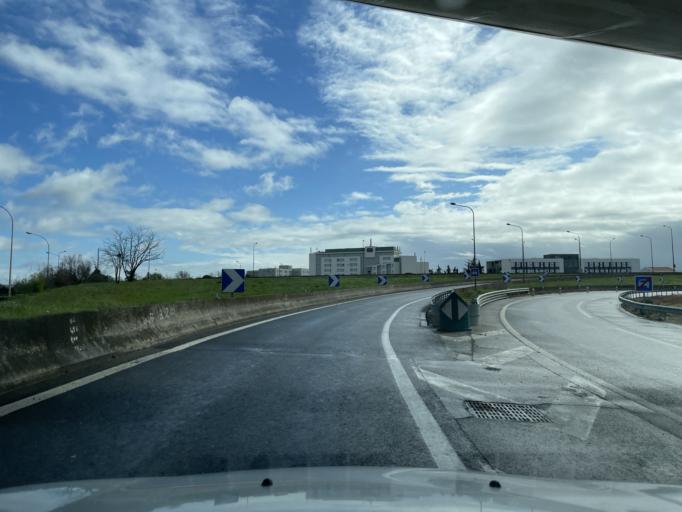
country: FR
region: Midi-Pyrenees
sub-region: Departement de la Haute-Garonne
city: Colomiers
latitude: 43.6086
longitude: 1.3673
